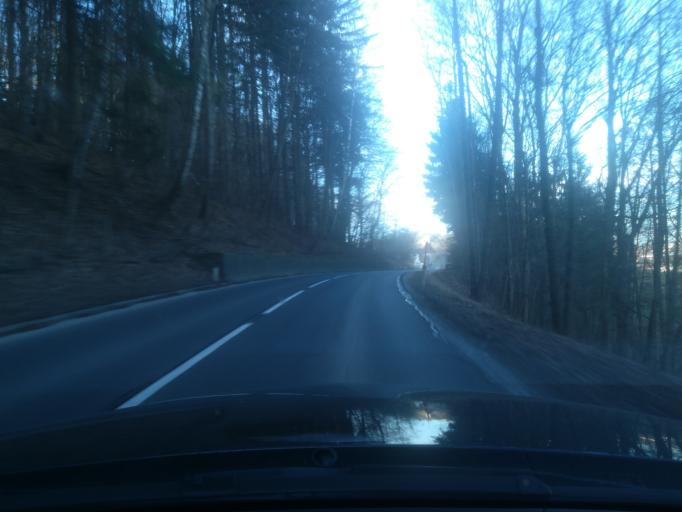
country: AT
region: Upper Austria
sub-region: Wels-Land
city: Marchtrenk
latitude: 48.1616
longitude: 14.0819
